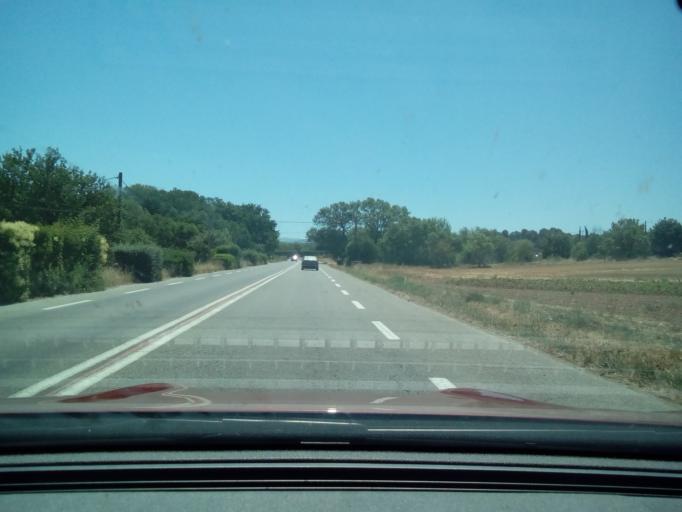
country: FR
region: Provence-Alpes-Cote d'Azur
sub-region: Departement des Bouches-du-Rhone
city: Chateauneuf-le-Rouge
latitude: 43.4750
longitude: 5.5748
